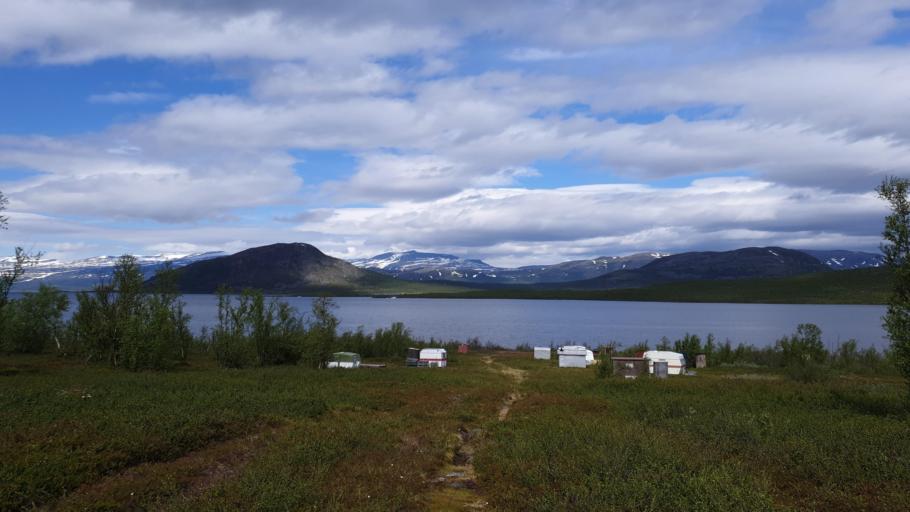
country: SE
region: Norrbotten
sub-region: Kiruna Kommun
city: Kiruna
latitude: 68.2334
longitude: 19.6192
